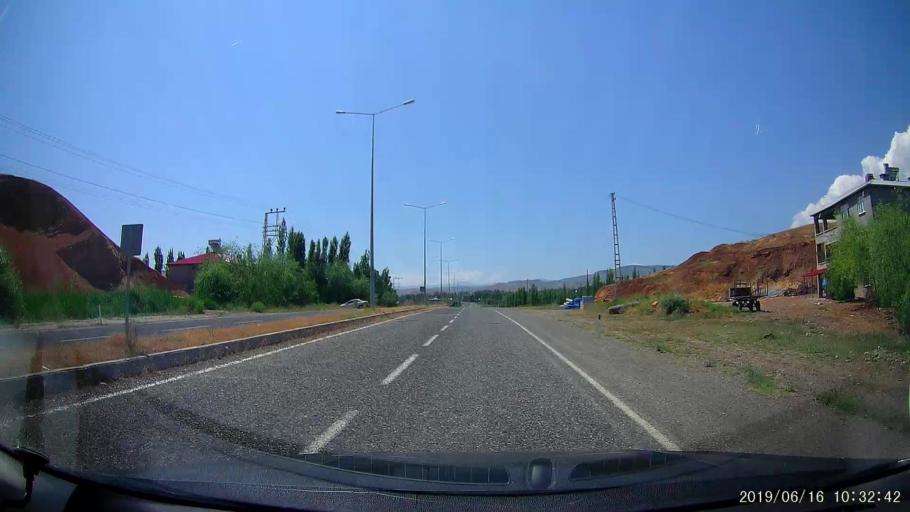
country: TR
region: Igdir
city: Tuzluca
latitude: 40.0479
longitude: 43.6540
